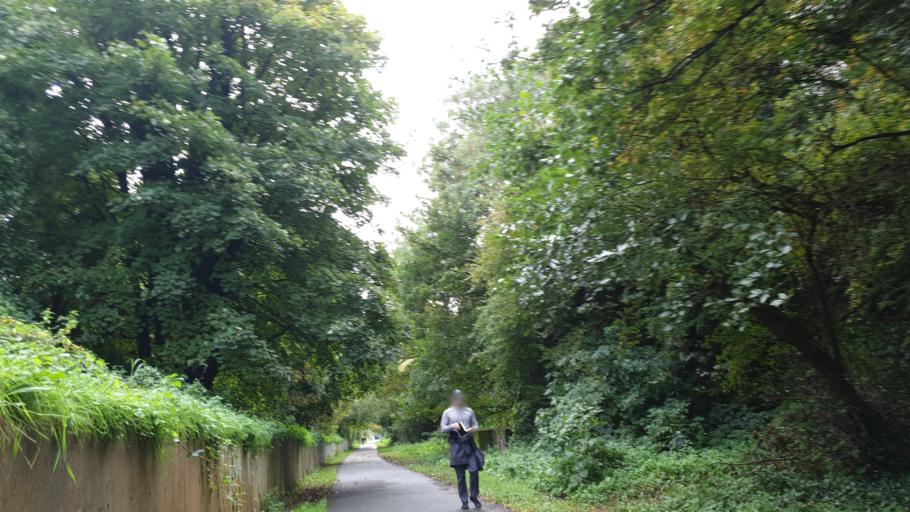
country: IE
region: Munster
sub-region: County Cork
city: Cork
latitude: 51.8950
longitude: -8.4170
